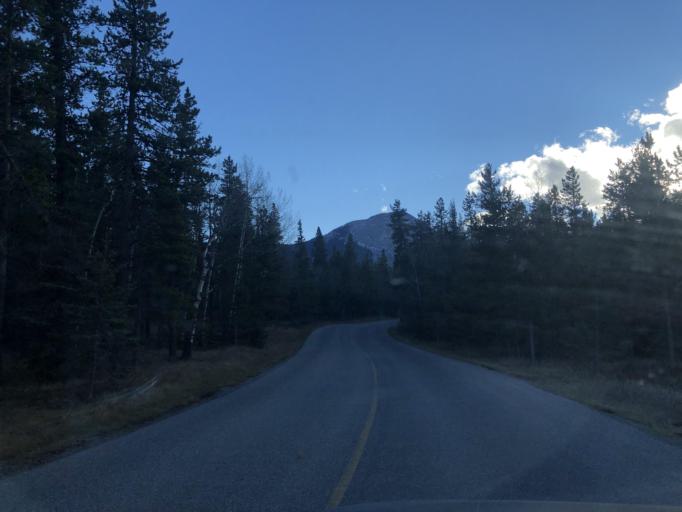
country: CA
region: Alberta
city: Canmore
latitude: 51.0774
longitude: -115.0783
